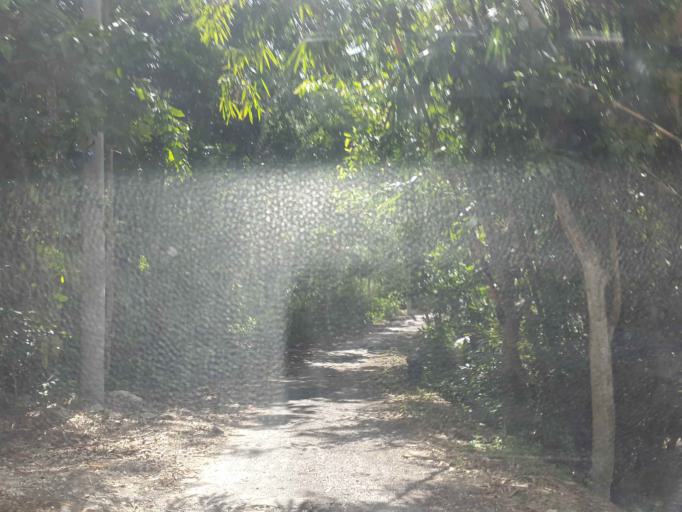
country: ID
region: Bali
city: Tanjung
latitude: -8.7561
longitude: 115.5337
